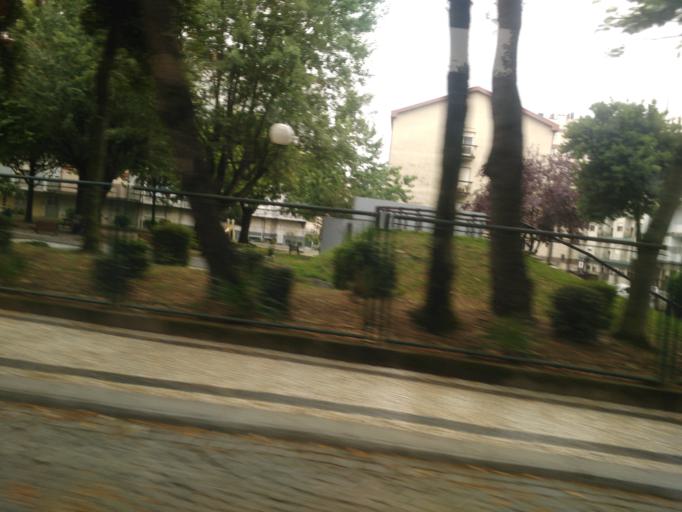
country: PT
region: Braga
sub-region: Braga
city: Braga
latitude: 41.5479
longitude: -8.4194
